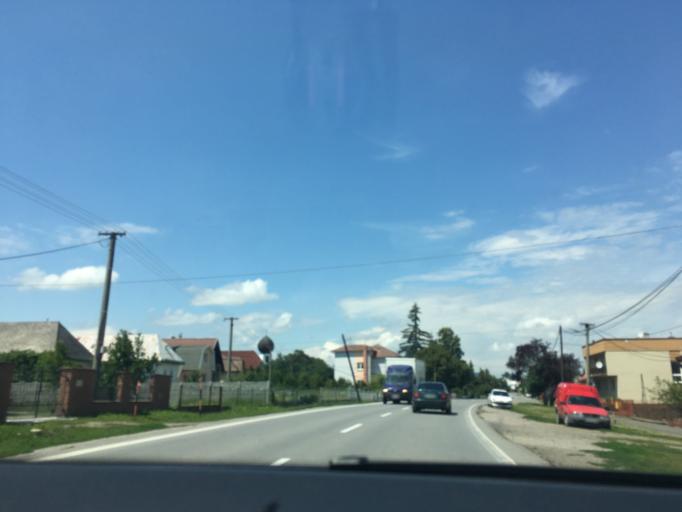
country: SK
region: Kosicky
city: Secovce
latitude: 48.7840
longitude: 21.6822
